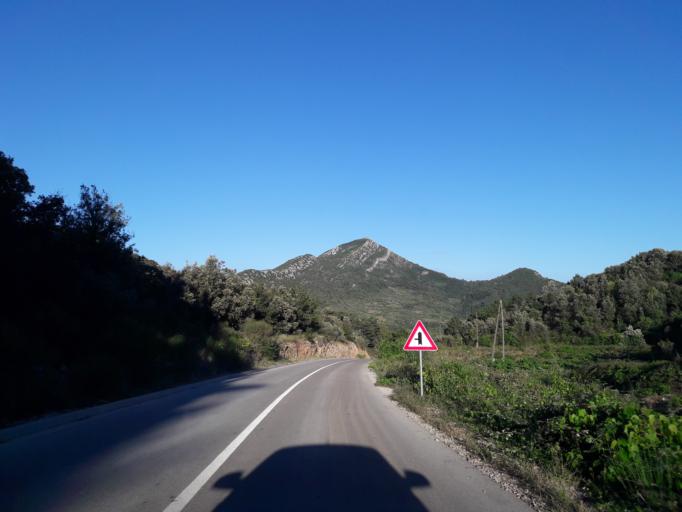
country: HR
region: Dubrovacko-Neretvanska
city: Orebic
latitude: 42.9985
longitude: 17.2600
